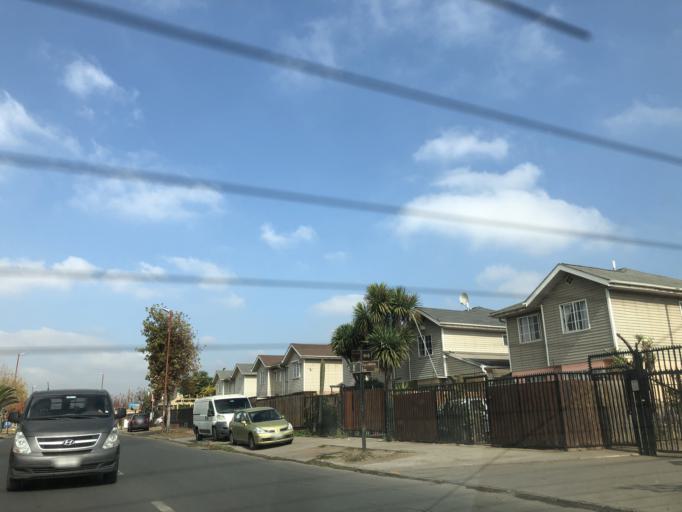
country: CL
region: Santiago Metropolitan
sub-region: Provincia de Cordillera
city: Puente Alto
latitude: -33.5942
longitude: -70.5850
